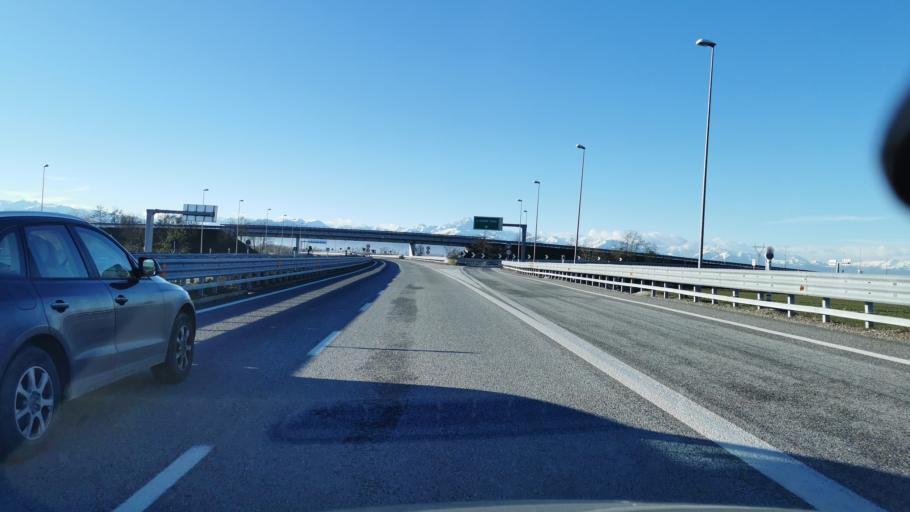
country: IT
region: Piedmont
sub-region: Provincia di Cuneo
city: Montanera
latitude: 44.4765
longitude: 7.6929
